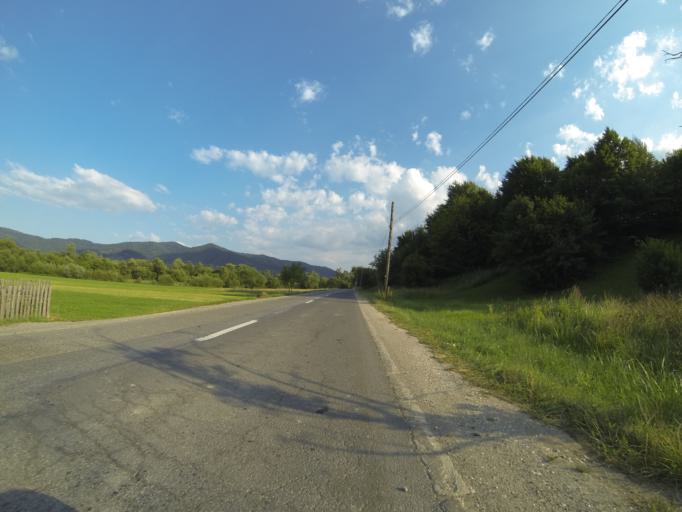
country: RO
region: Brasov
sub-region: Comuna Sinca Noua
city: Sinca Noua
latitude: 45.7180
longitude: 25.2405
